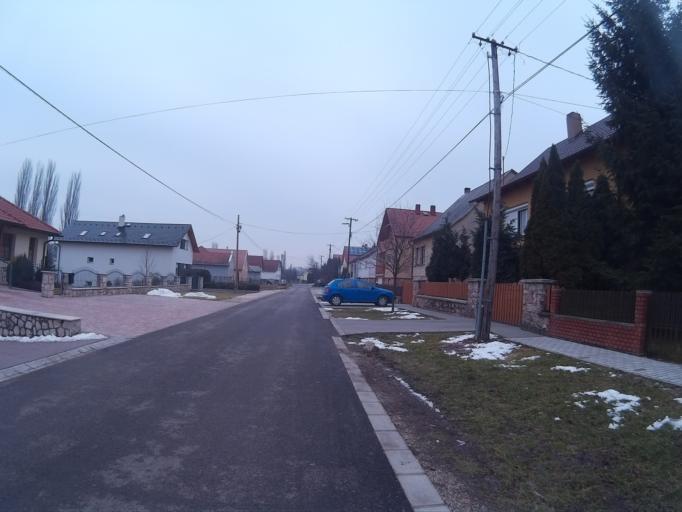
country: HU
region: Komarom-Esztergom
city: Tarjan
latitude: 47.6058
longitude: 18.5148
